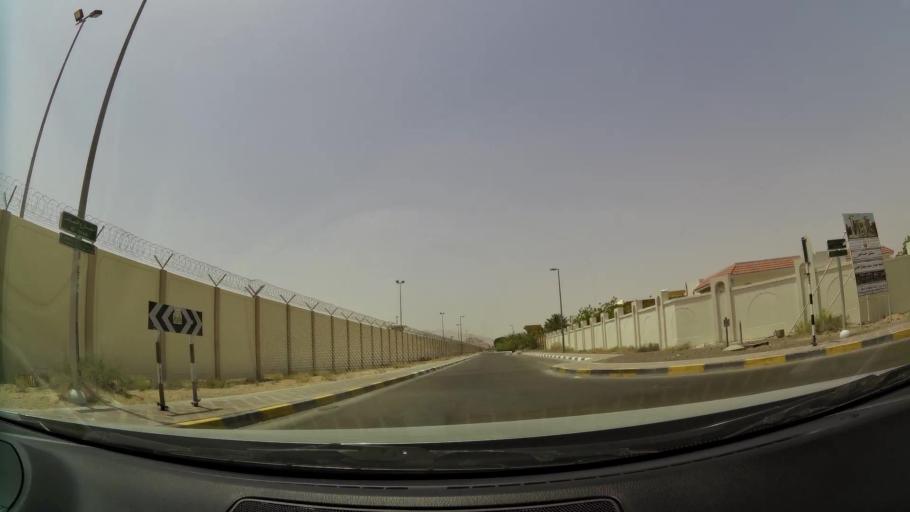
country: AE
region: Abu Dhabi
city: Al Ain
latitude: 24.1938
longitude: 55.7423
